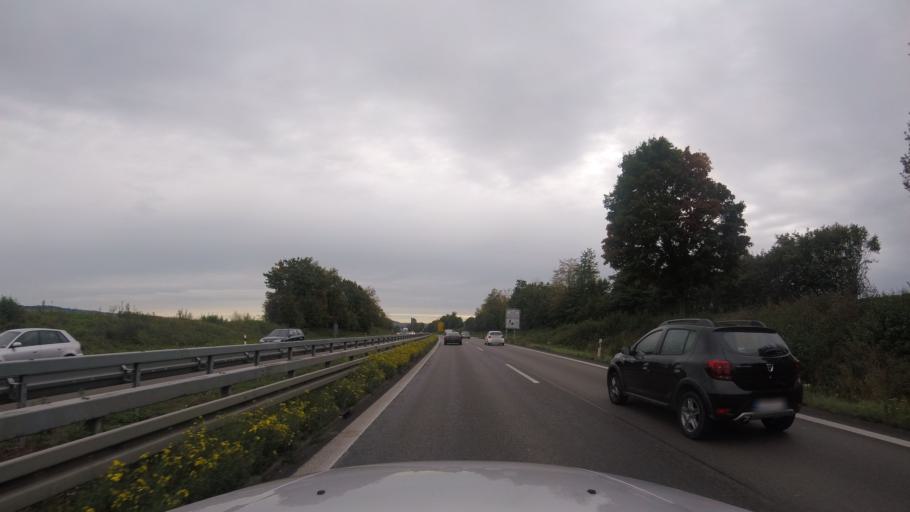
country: DE
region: Baden-Wuerttemberg
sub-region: Regierungsbezirk Stuttgart
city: Waiblingen
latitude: 48.8161
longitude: 9.3369
